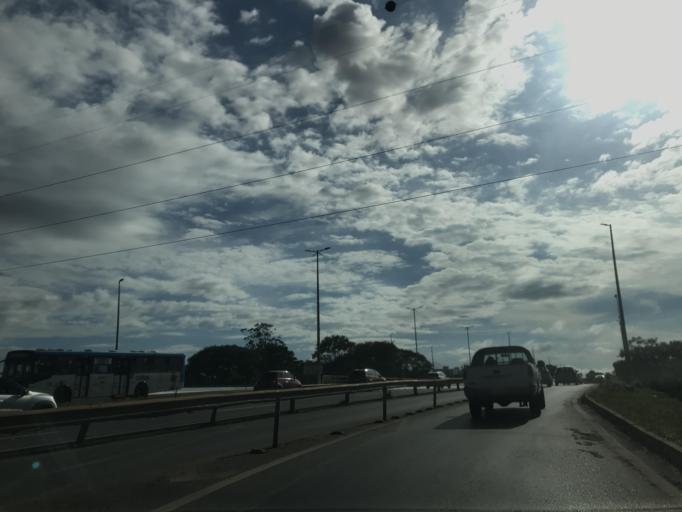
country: BR
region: Federal District
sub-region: Brasilia
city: Brasilia
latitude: -15.8111
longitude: -47.9514
